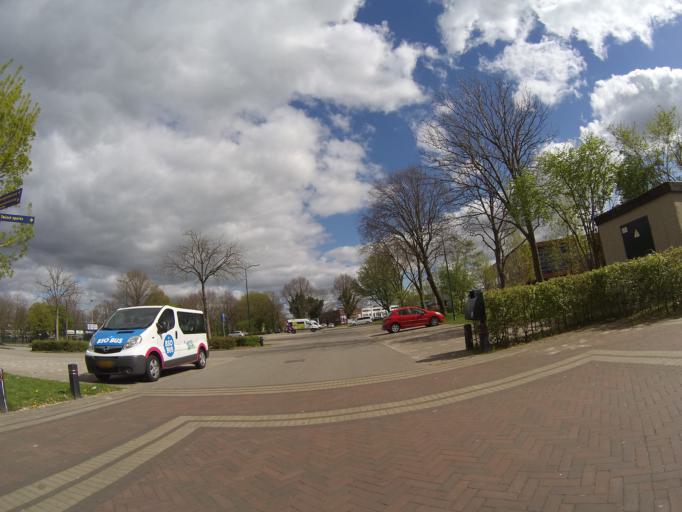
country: NL
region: Utrecht
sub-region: Gemeente Bunschoten
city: Spakenburg
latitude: 52.2337
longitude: 5.3638
